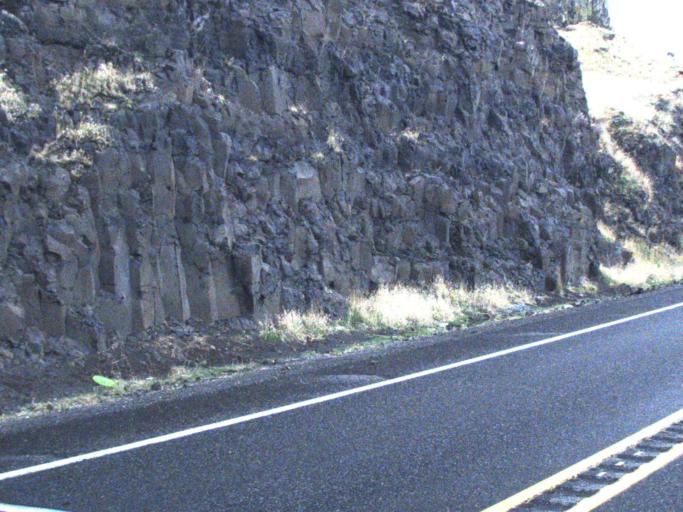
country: US
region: Washington
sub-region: Benton County
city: Finley
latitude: 46.0457
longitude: -118.9398
